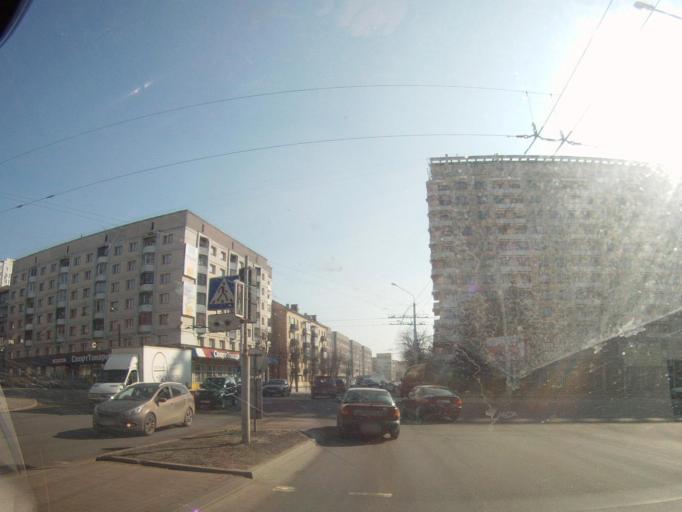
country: BY
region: Minsk
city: Minsk
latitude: 53.9263
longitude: 27.5935
